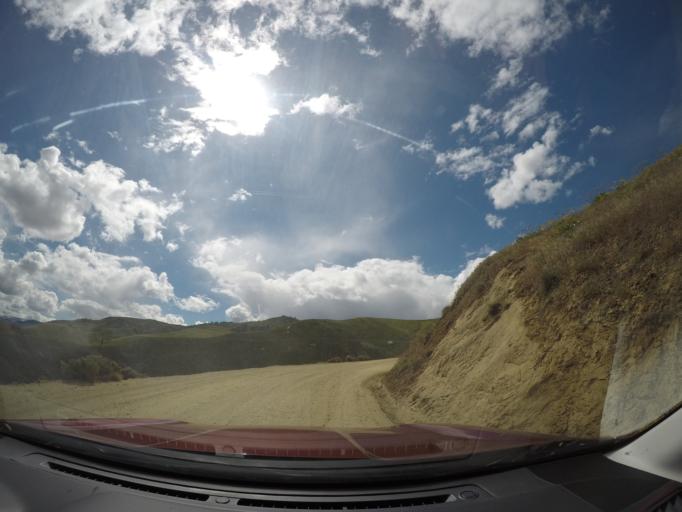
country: US
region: Washington
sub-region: Chelan County
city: West Wenatchee
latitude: 47.4632
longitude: -120.3726
